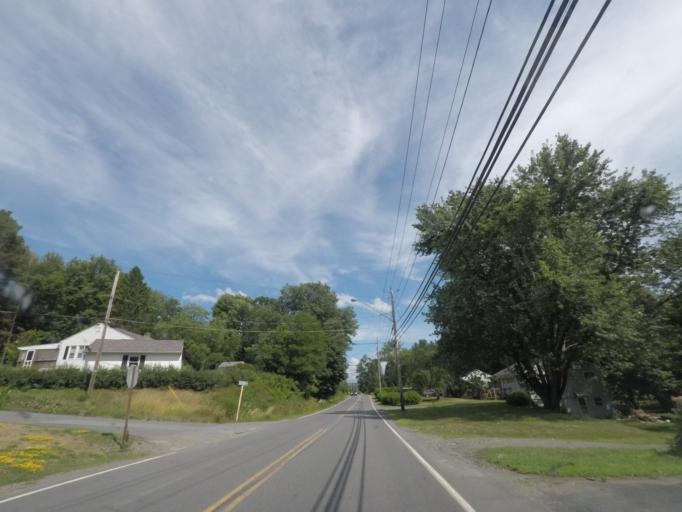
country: US
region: New York
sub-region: Rensselaer County
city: Poestenkill
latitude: 42.6955
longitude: -73.6027
